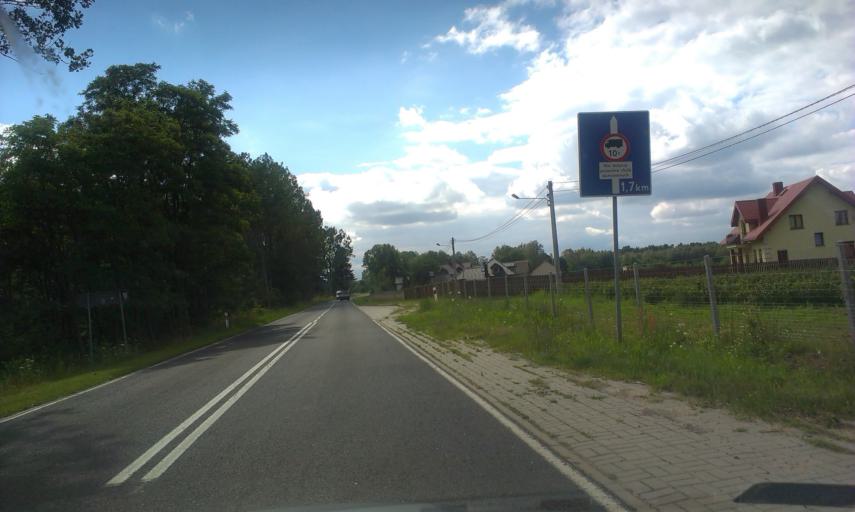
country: PL
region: Lodz Voivodeship
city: Zabia Wola
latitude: 51.9660
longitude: 20.6756
